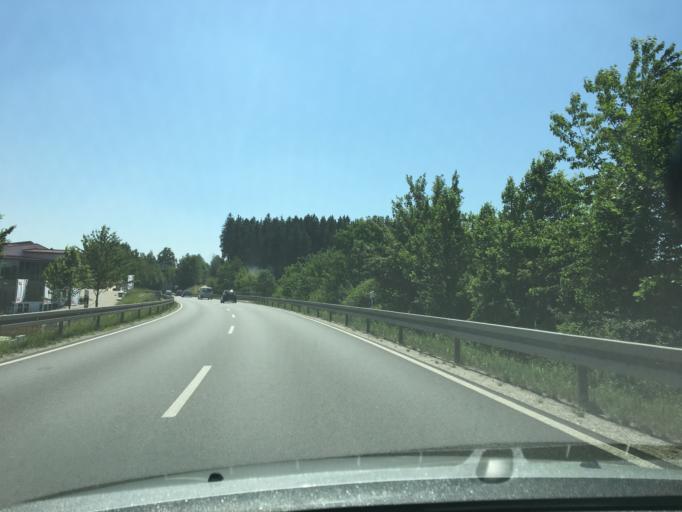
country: DE
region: Bavaria
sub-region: Lower Bavaria
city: Vilsbiburg
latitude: 48.4514
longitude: 12.3336
